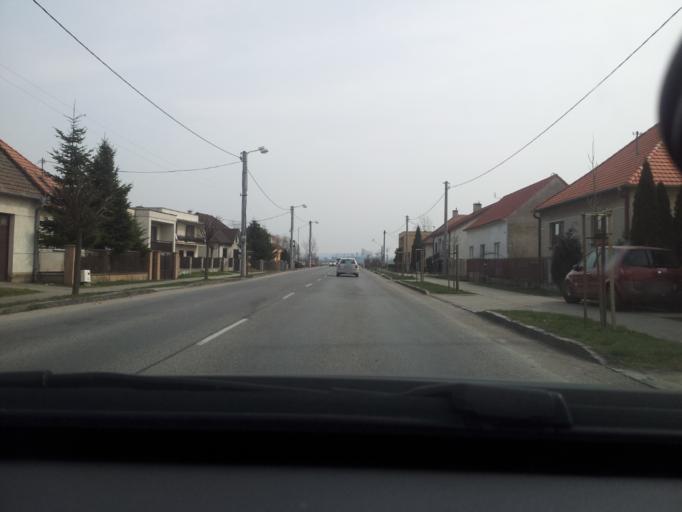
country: SK
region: Trnavsky
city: Leopoldov
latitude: 48.4398
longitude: 17.7187
